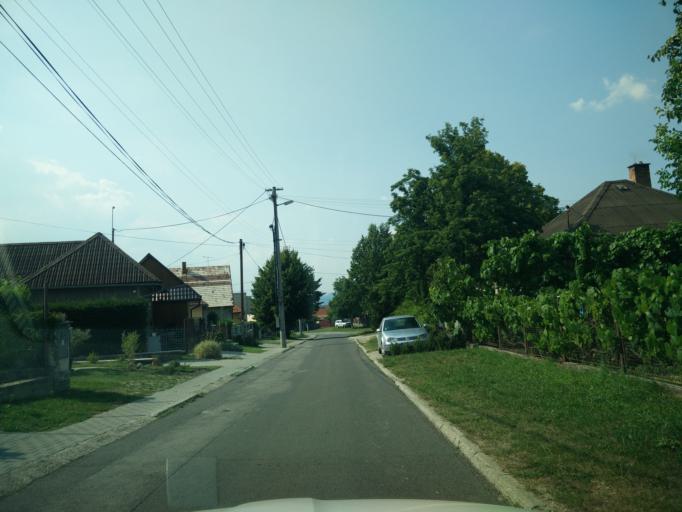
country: SK
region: Nitriansky
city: Prievidza
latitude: 48.7291
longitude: 18.6276
